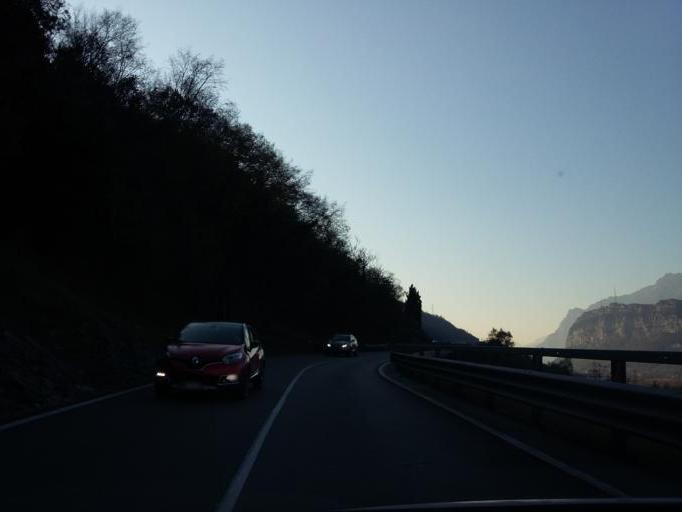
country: IT
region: Trentino-Alto Adige
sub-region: Provincia di Trento
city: Bolognano-Vignole
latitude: 45.9051
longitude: 10.9017
